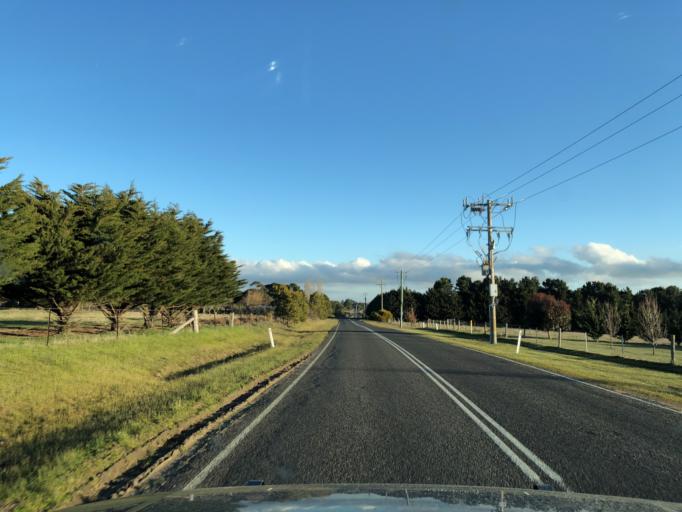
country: AU
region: Victoria
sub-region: Moorabool
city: Bacchus Marsh
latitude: -37.5828
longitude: 144.2373
